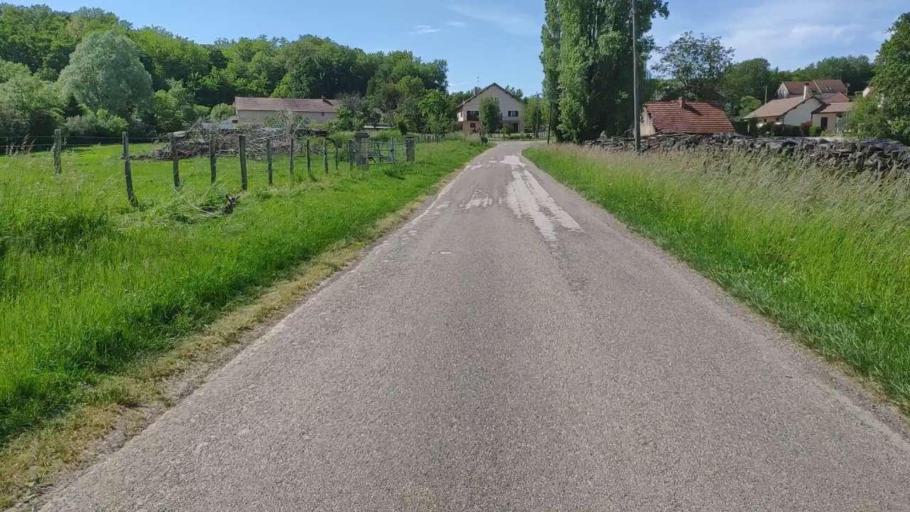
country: FR
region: Franche-Comte
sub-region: Departement du Jura
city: Bletterans
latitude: 46.7681
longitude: 5.4747
